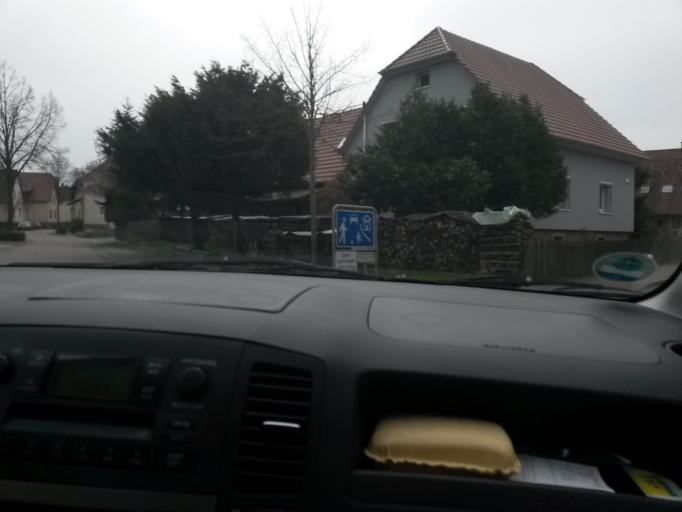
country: DE
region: Baden-Wuerttemberg
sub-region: Freiburg Region
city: Kippenheim
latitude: 48.3177
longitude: 7.8087
